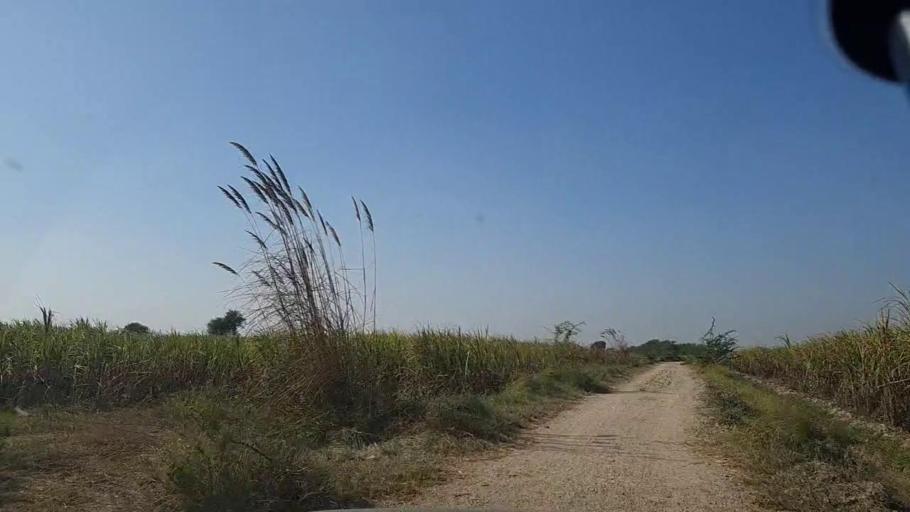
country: PK
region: Sindh
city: Chuhar Jamali
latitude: 24.5745
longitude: 68.0417
